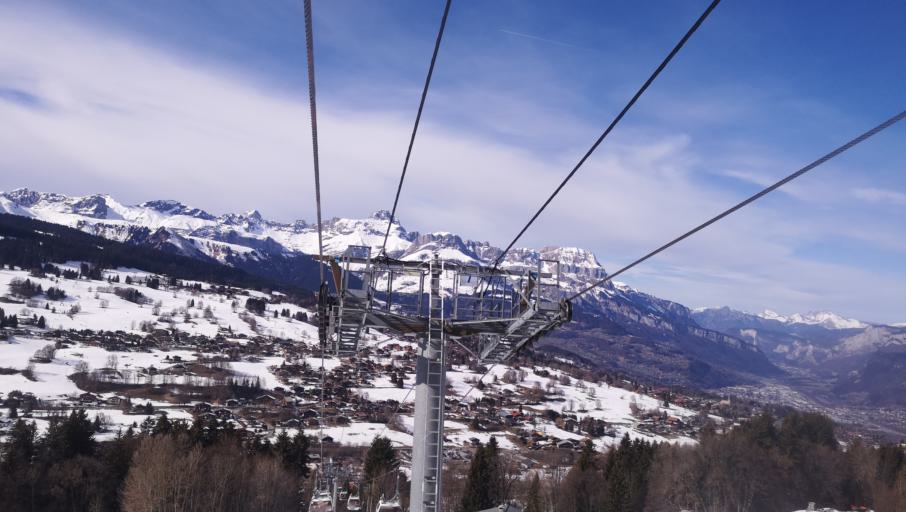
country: FR
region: Rhone-Alpes
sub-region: Departement de la Haute-Savoie
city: Combloux
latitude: 45.8747
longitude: 6.6480
